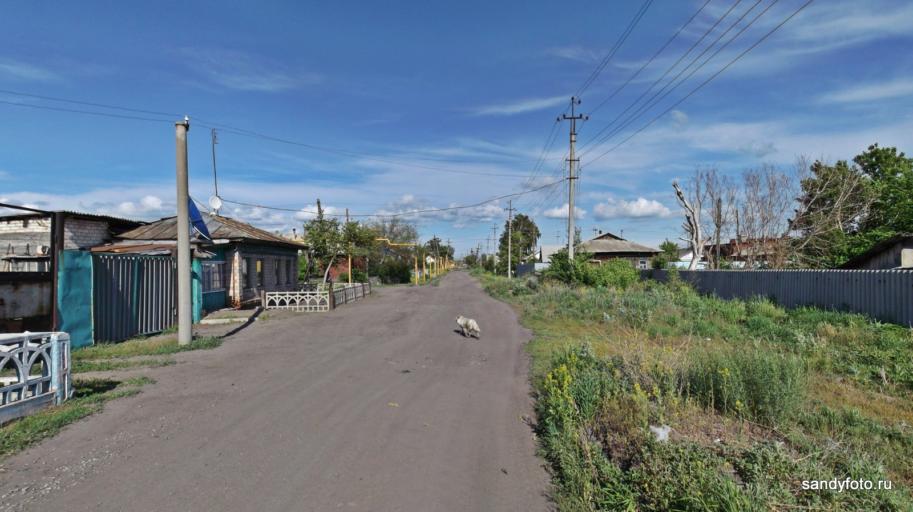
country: RU
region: Chelyabinsk
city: Troitsk
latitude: 54.0934
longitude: 61.5861
